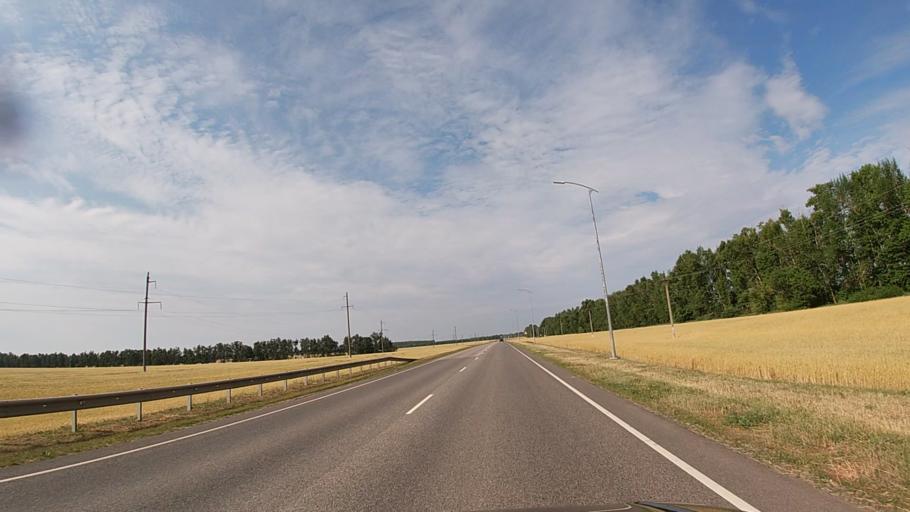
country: RU
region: Belgorod
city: Proletarskiy
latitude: 50.8158
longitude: 35.7520
